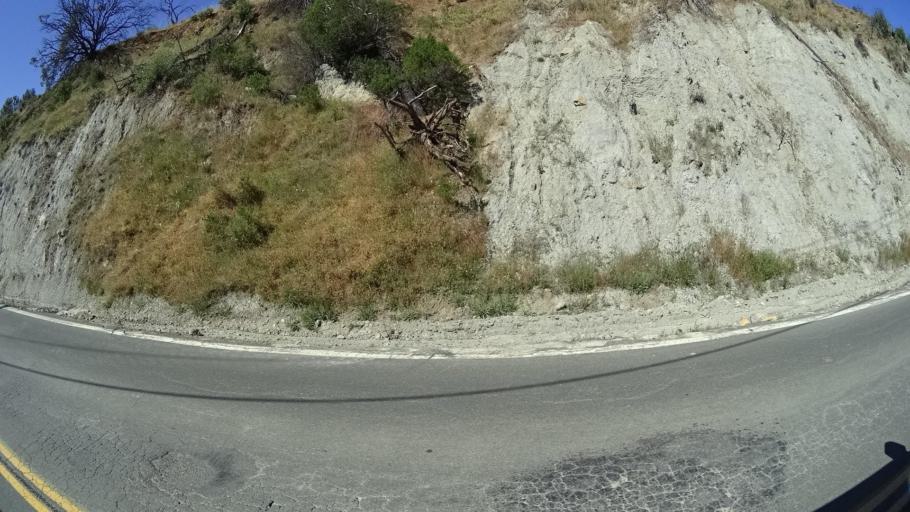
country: US
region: California
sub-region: Lake County
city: Clearlake
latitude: 39.0231
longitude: -122.5737
